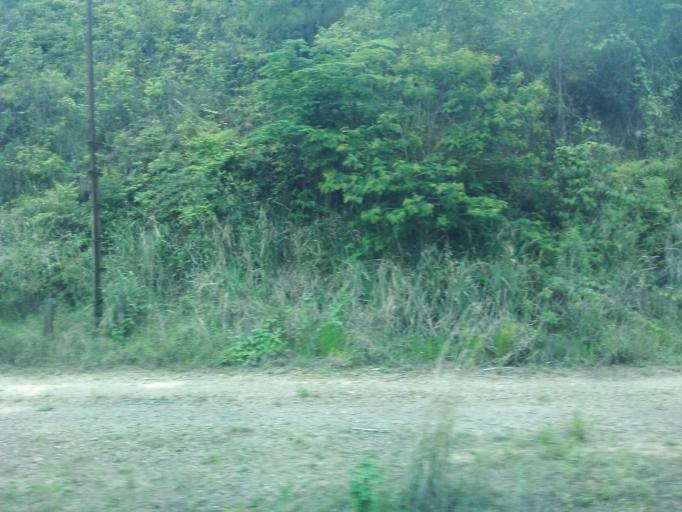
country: BR
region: Minas Gerais
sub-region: Nova Era
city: Nova Era
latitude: -19.7307
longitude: -42.9837
